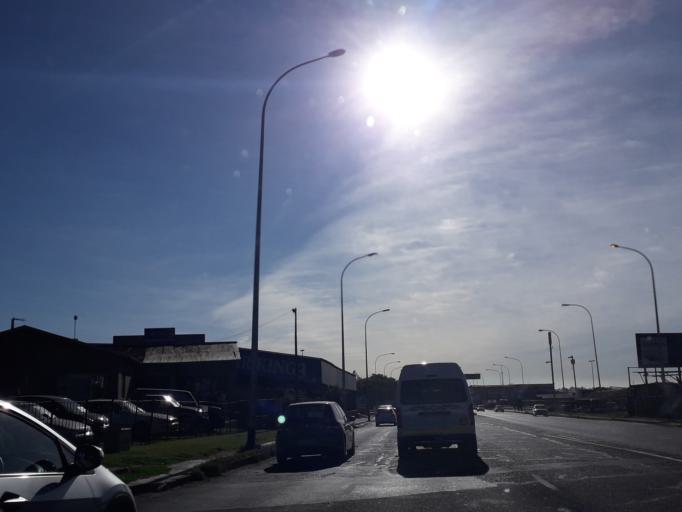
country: ZA
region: Gauteng
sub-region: City of Johannesburg Metropolitan Municipality
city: Roodepoort
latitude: -26.1731
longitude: 27.9422
